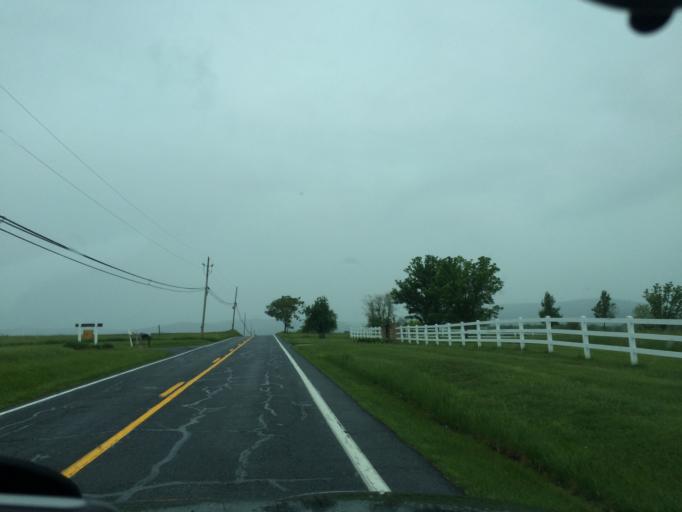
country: US
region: Maryland
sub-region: Frederick County
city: Thurmont
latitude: 39.6149
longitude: -77.3651
